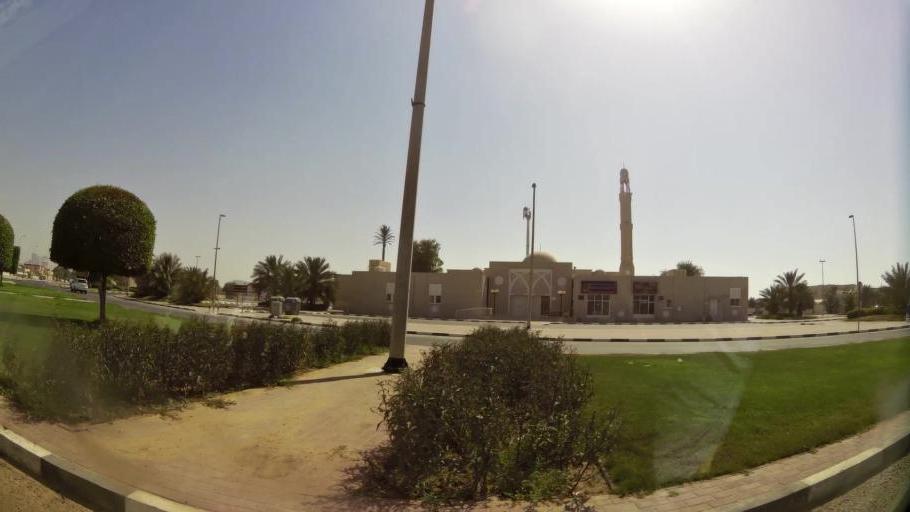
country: AE
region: Ajman
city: Ajman
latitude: 25.4156
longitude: 55.4723
